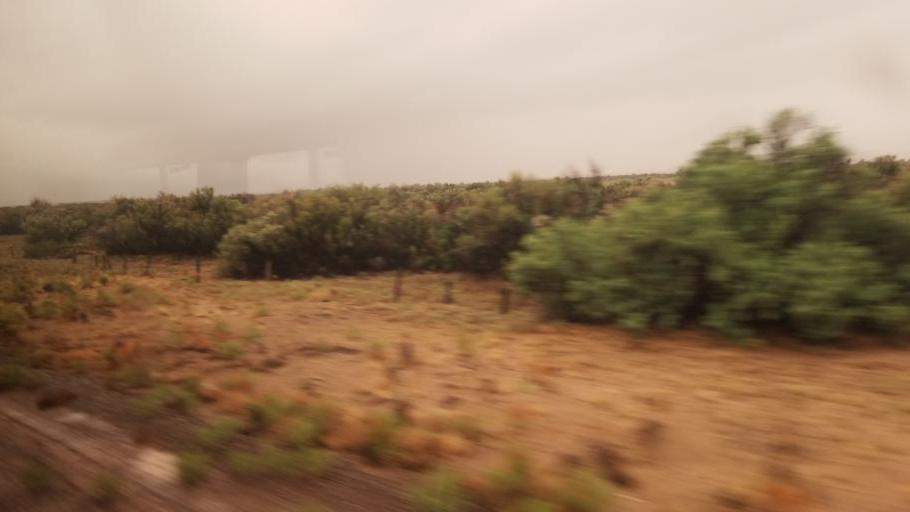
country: US
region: Arizona
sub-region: Navajo County
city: Joseph City
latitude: 34.9674
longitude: -110.4574
